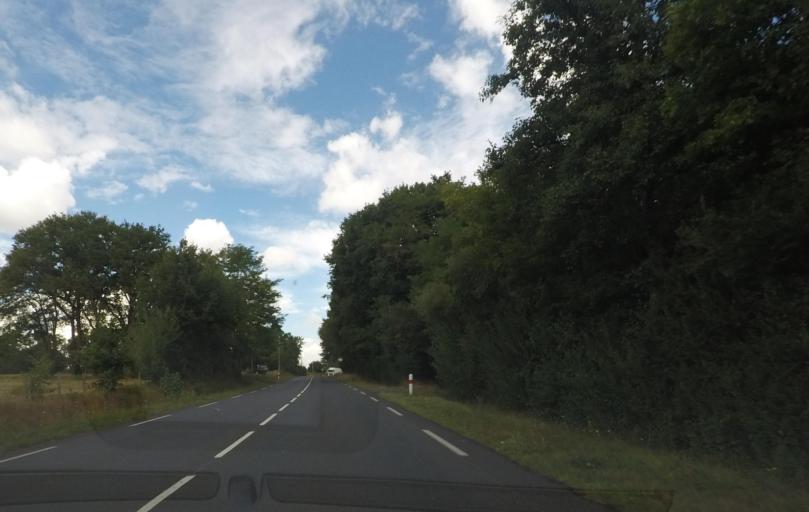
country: FR
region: Pays de la Loire
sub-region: Departement de la Sarthe
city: Champagne
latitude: 48.0628
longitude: 0.2912
